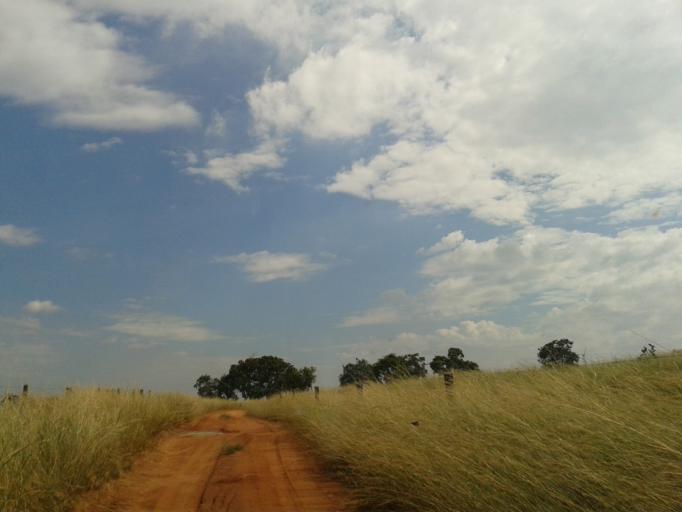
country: BR
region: Minas Gerais
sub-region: Campina Verde
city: Campina Verde
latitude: -19.3924
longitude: -49.6424
